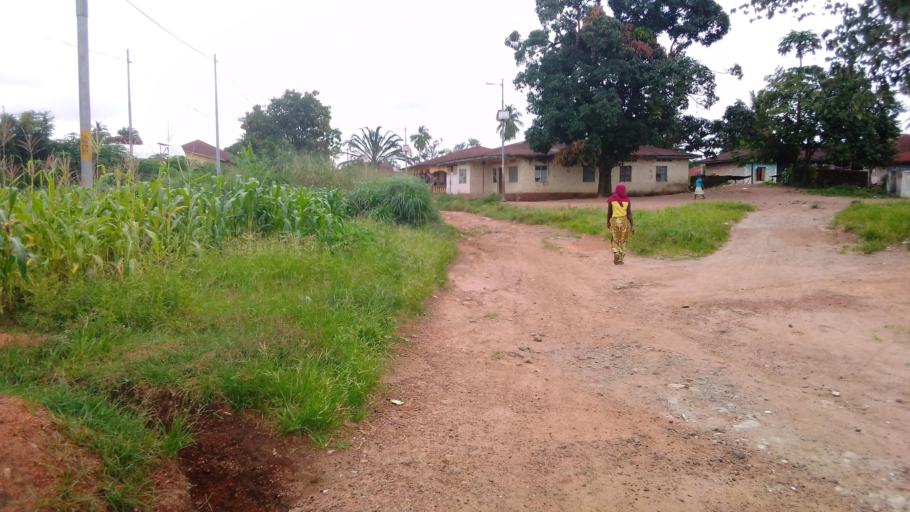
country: SL
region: Northern Province
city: Makeni
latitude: 8.8793
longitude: -12.0445
